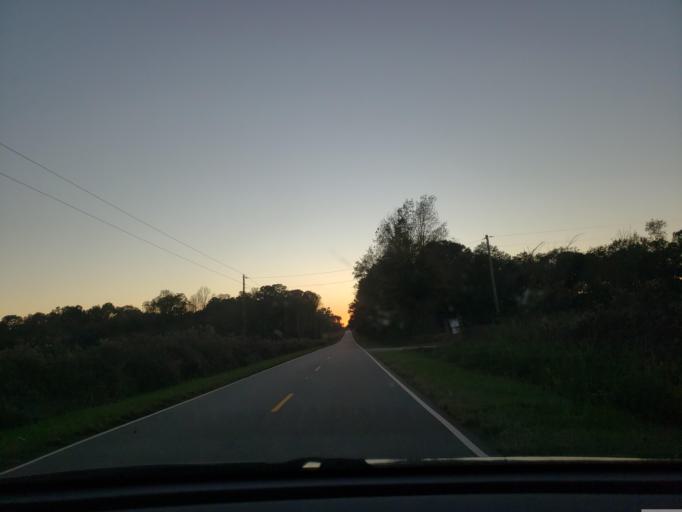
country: US
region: North Carolina
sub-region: Duplin County
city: Beulaville
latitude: 34.7581
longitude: -77.6853
